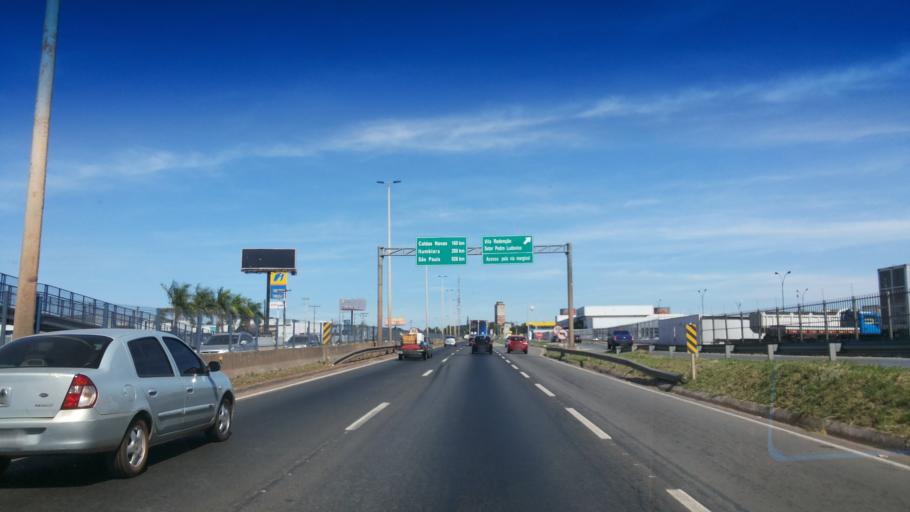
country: BR
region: Goias
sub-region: Goiania
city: Goiania
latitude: -16.7153
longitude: -49.2353
